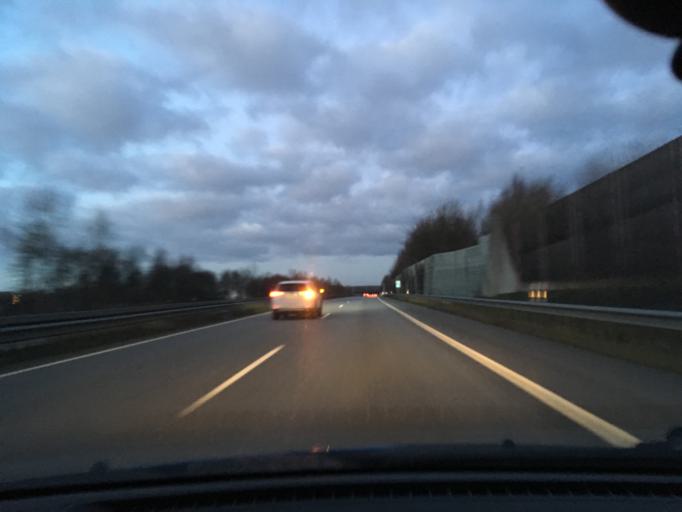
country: DE
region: Schleswig-Holstein
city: Heiligenstedten
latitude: 53.9509
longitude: 9.4883
